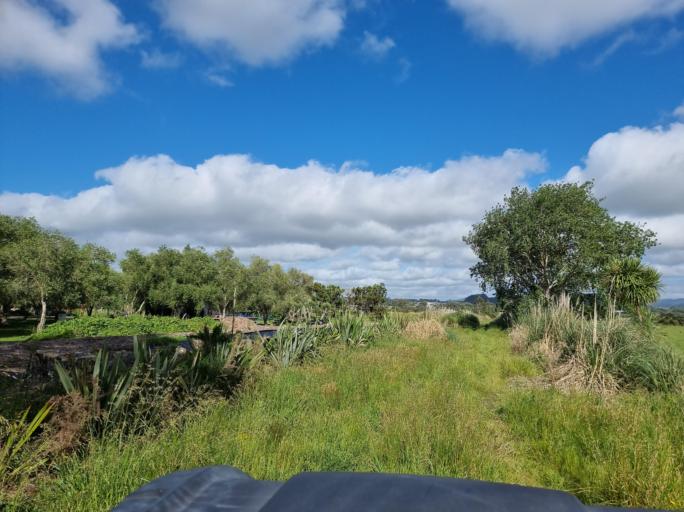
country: NZ
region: Auckland
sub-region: Auckland
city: Wellsford
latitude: -36.1256
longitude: 174.5878
